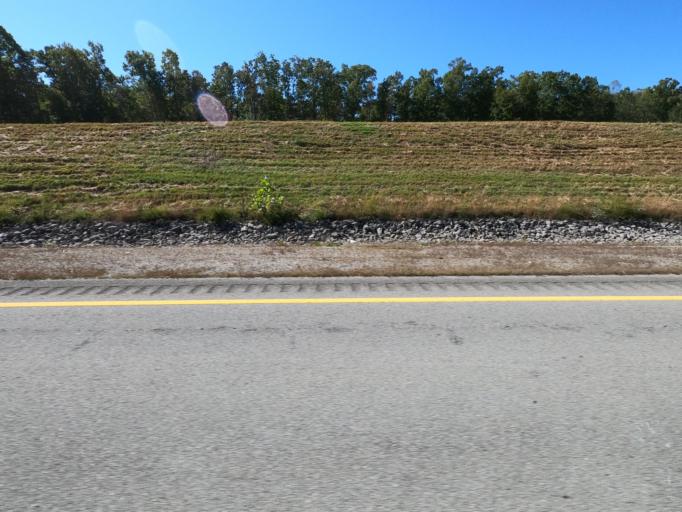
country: US
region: Tennessee
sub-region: Williamson County
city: Fairview
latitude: 35.8884
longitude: -87.1135
